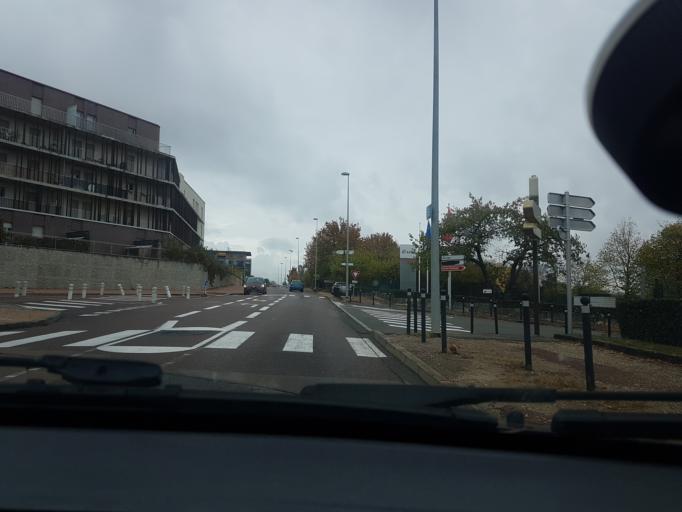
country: FR
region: Bourgogne
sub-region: Departement de la Cote-d'Or
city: Saint-Apollinaire
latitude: 47.3233
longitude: 5.0735
